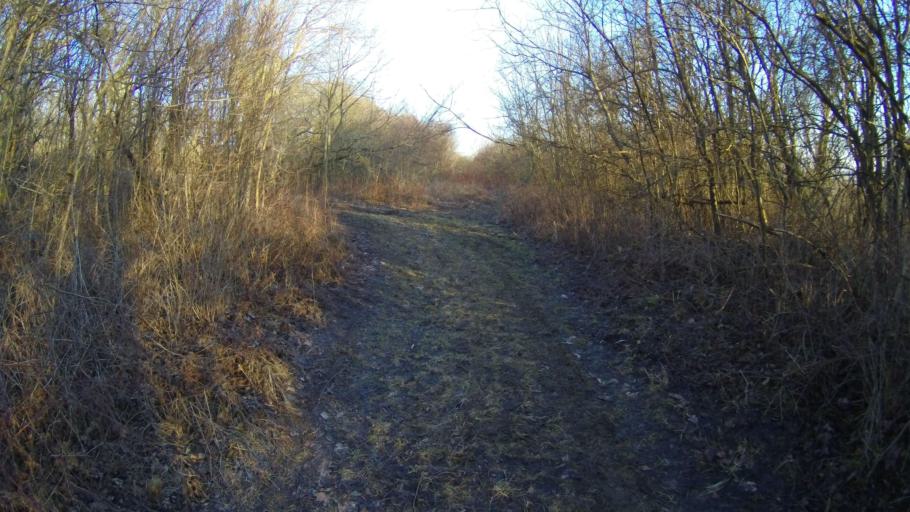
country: CZ
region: Ustecky
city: Roudnice nad Labem
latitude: 50.3808
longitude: 14.2851
